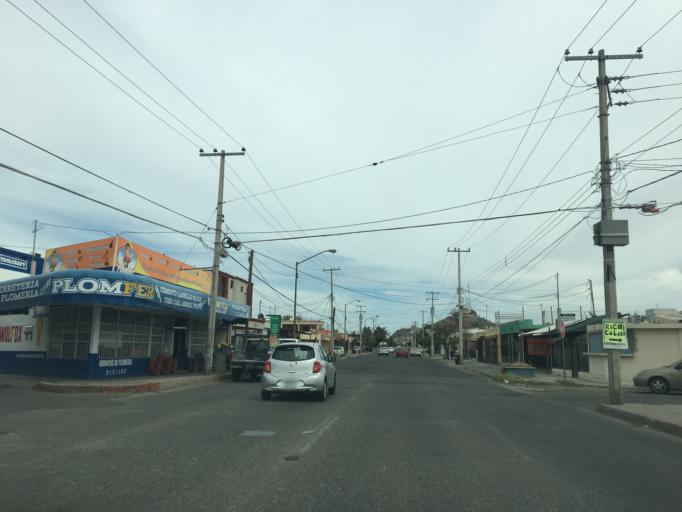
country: MX
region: Sonora
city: Hermosillo
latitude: 29.0733
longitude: -110.9732
